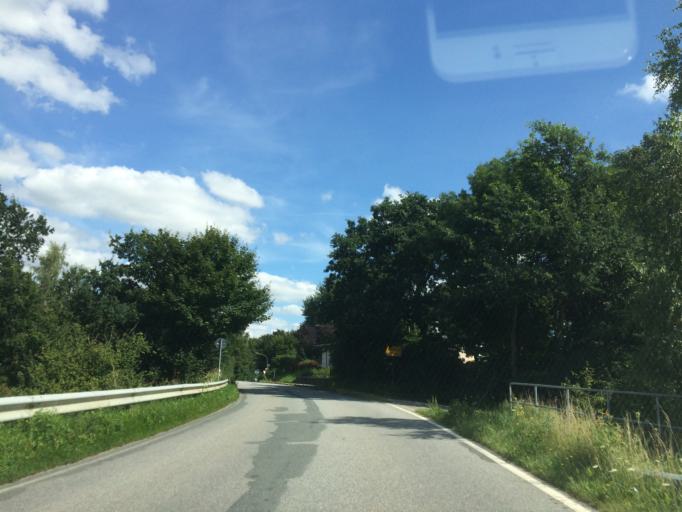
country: DE
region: Schleswig-Holstein
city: Grebin
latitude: 54.1975
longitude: 10.4863
